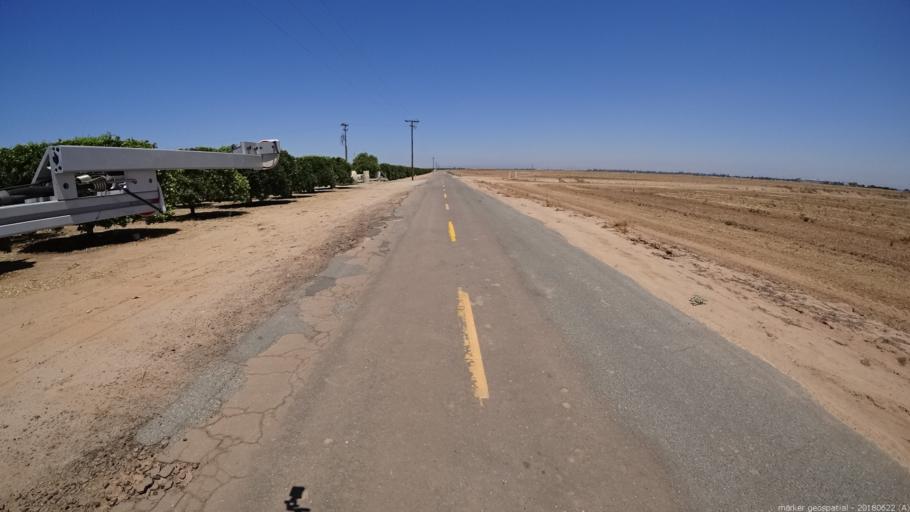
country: US
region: California
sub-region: Fresno County
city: Clovis
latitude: 36.8695
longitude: -119.8205
